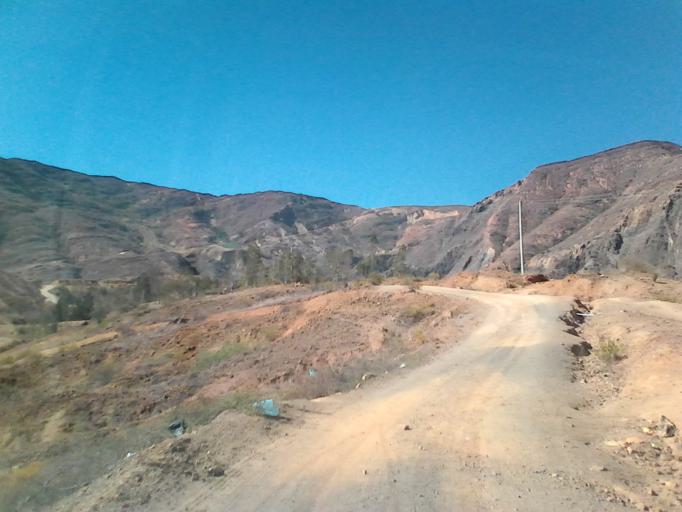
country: CO
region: Boyaca
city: Sachica
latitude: 5.5614
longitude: -73.5480
